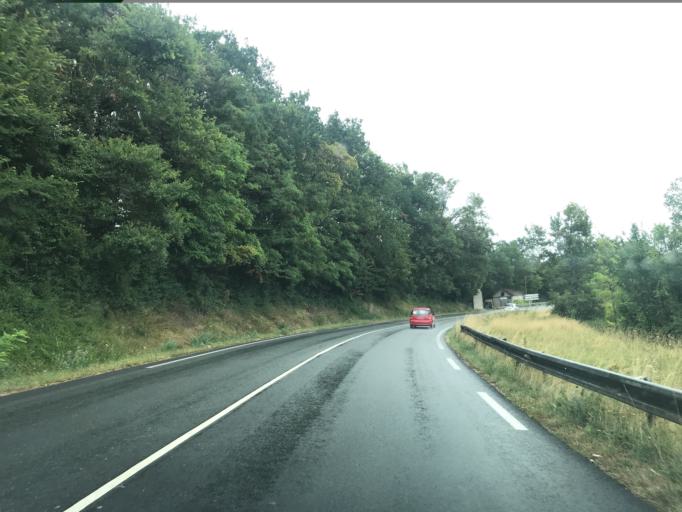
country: FR
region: Aquitaine
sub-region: Departement de la Dordogne
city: Brantome
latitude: 45.3067
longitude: 0.6619
